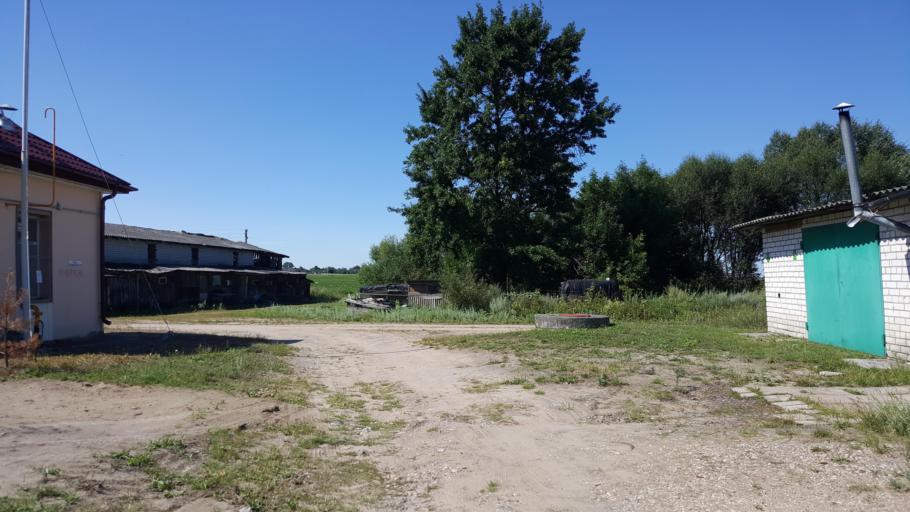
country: BY
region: Brest
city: Charnawchytsy
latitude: 52.2146
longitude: 23.7537
